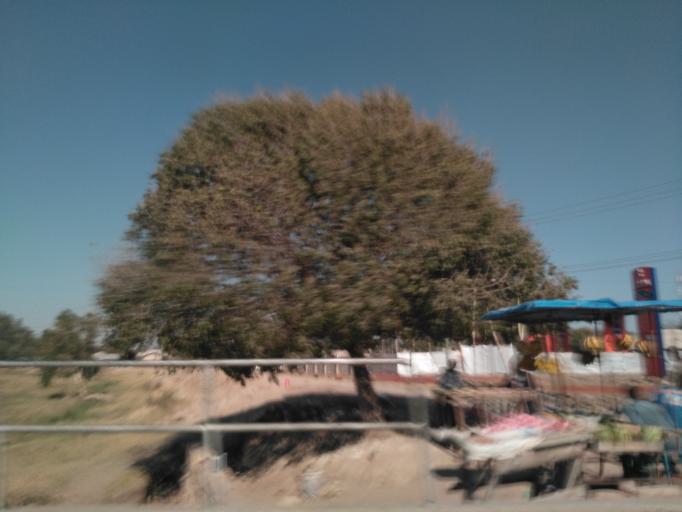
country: TZ
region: Dodoma
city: Dodoma
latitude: -6.1532
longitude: 35.7476
